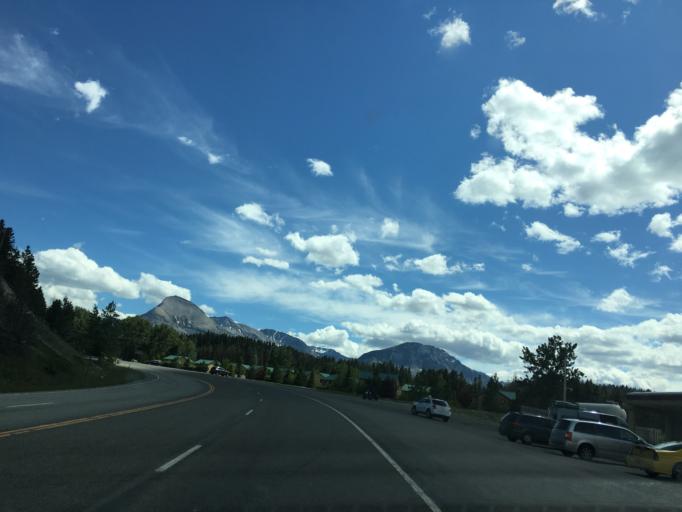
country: US
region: Montana
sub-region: Glacier County
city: North Browning
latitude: 48.7425
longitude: -113.4293
